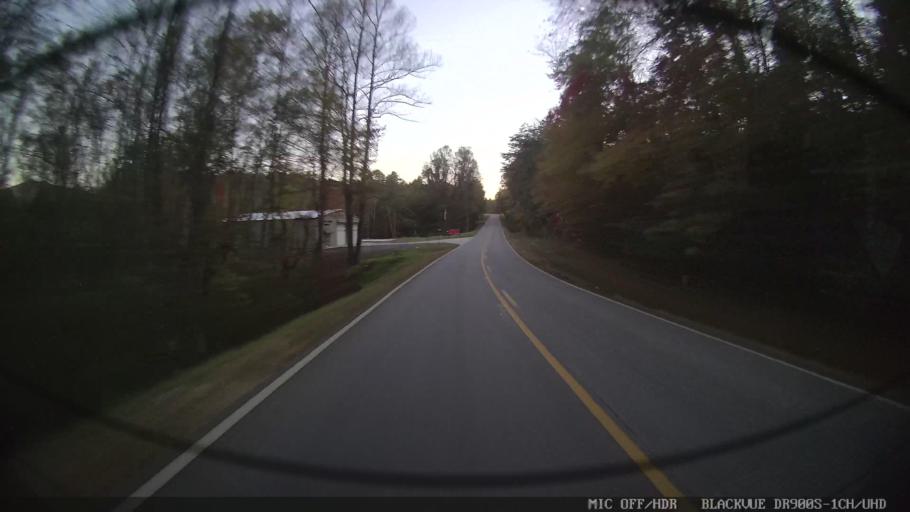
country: US
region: Georgia
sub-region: Towns County
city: Hiawassee
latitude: 34.9489
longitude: -83.8588
